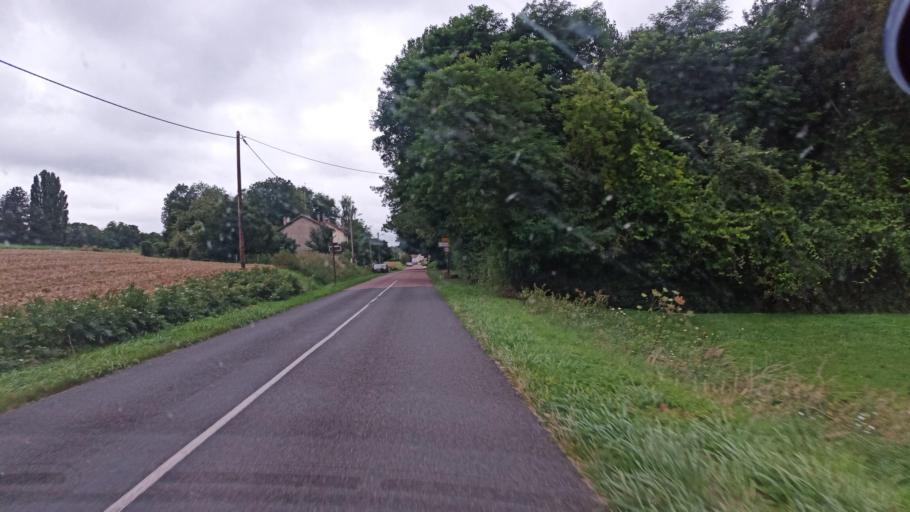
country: FR
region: Ile-de-France
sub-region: Departement de Seine-et-Marne
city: Voulx
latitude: 48.2782
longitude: 2.9790
